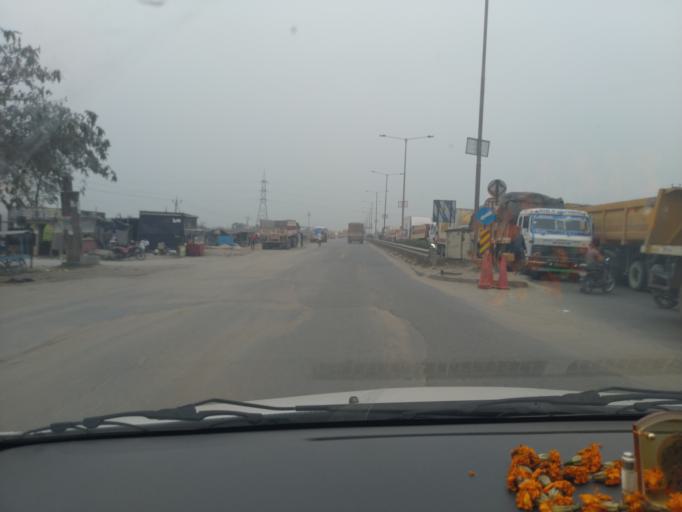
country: IN
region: Bihar
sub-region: Rohtas
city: Dehri
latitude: 24.9588
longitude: 83.9505
